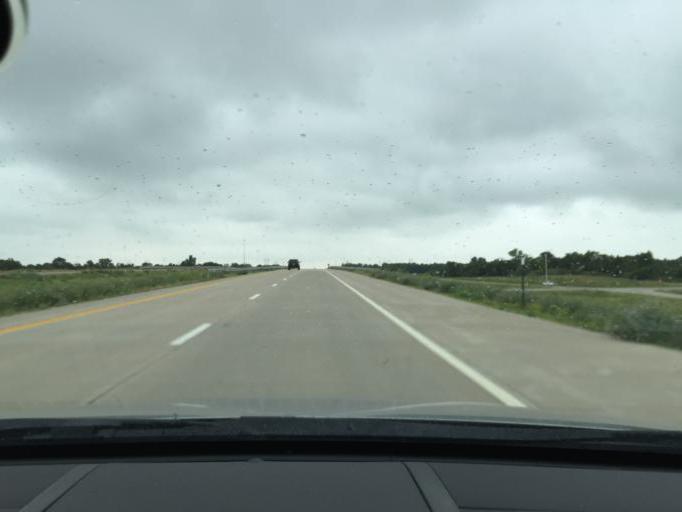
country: US
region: Kansas
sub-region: Reno County
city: Hutchinson
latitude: 38.1175
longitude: -97.8758
